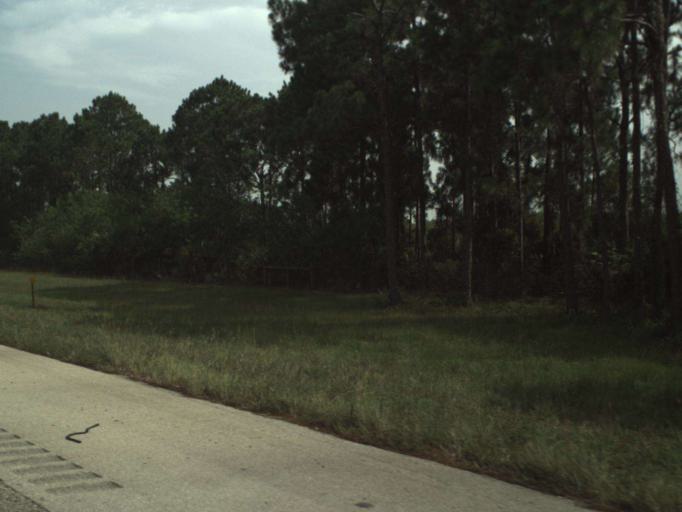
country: US
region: Florida
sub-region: Saint Lucie County
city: Port Saint Lucie
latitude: 27.2347
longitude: -80.4088
